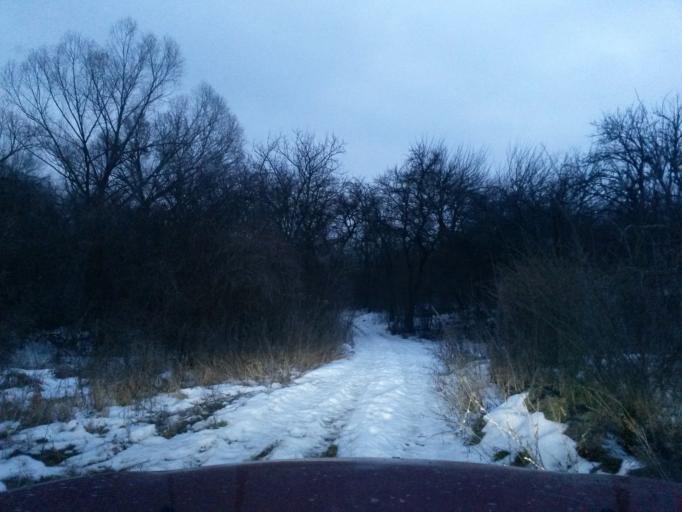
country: SK
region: Kosicky
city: Secovce
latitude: 48.7147
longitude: 21.6277
